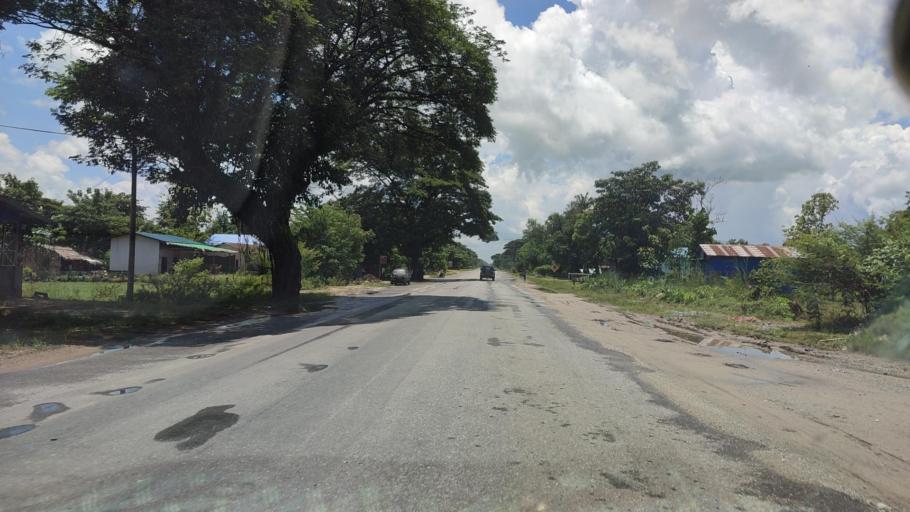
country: MM
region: Bago
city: Pyu
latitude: 18.5959
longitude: 96.4217
